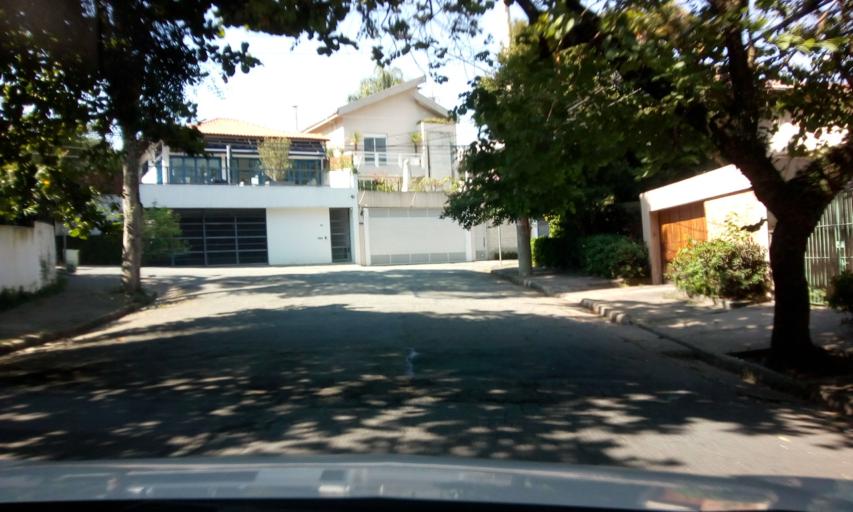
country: BR
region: Sao Paulo
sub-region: Sao Paulo
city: Sao Paulo
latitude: -23.5460
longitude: -46.6857
